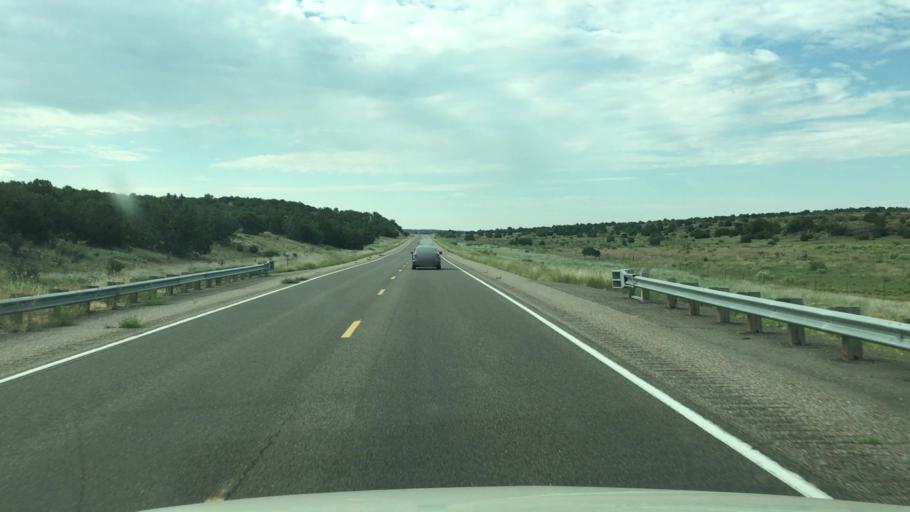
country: US
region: New Mexico
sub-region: Santa Fe County
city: Eldorado at Santa Fe
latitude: 35.3023
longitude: -105.8276
